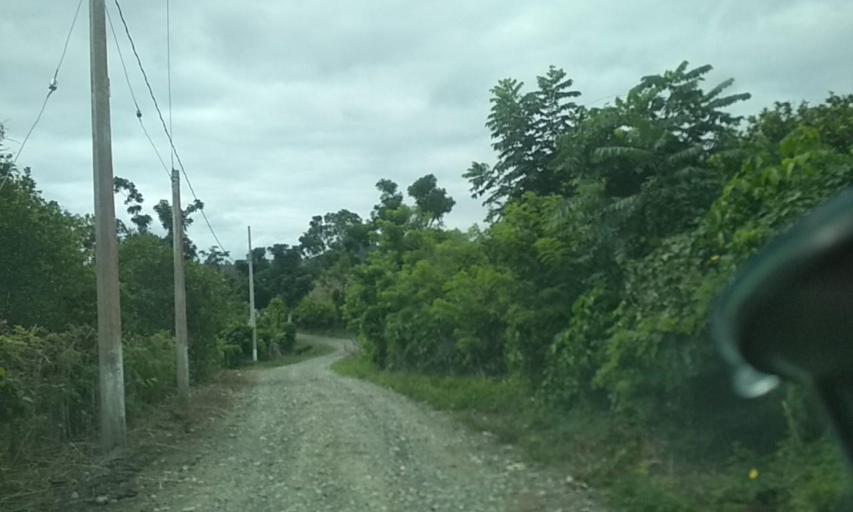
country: MX
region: Veracruz
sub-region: Papantla
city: Polutla
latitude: 20.5823
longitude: -97.2651
